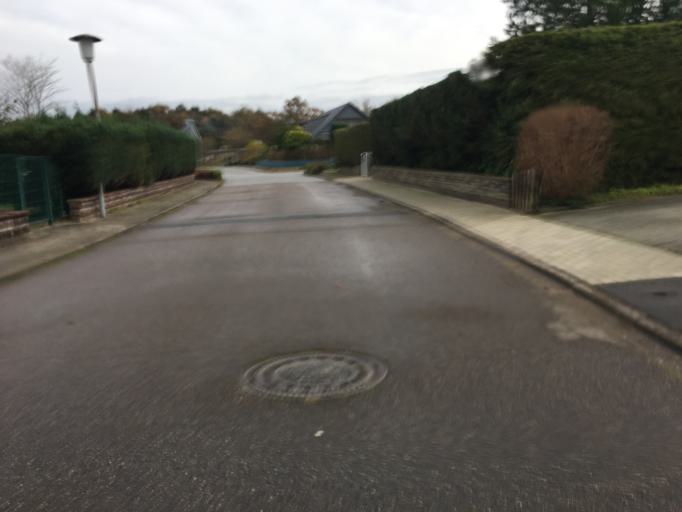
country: DE
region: Schleswig-Holstein
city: Wanderup
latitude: 54.6910
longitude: 9.3365
